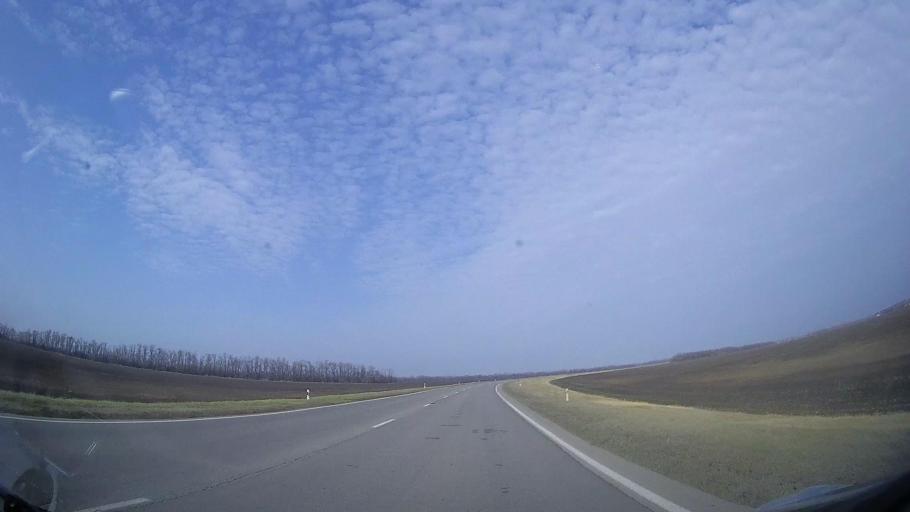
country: RU
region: Rostov
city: Tselina
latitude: 46.5134
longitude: 41.0002
